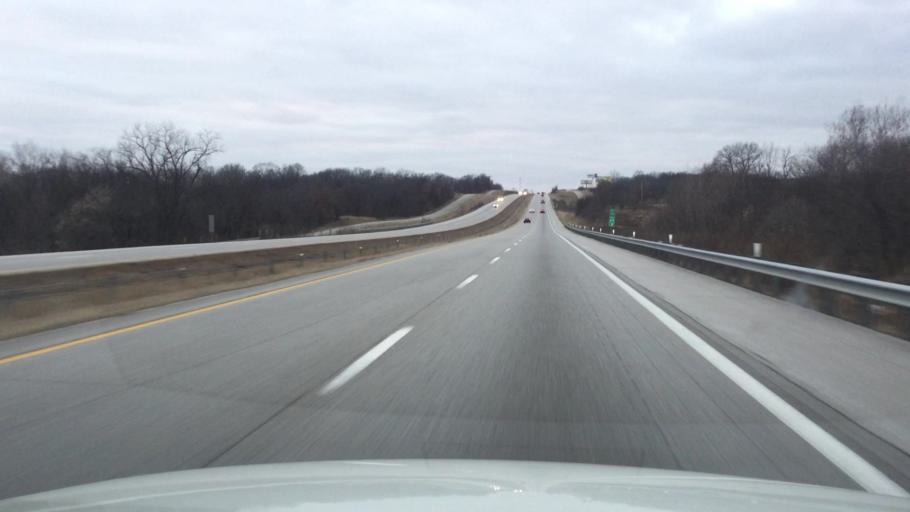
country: US
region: Missouri
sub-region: Saline County
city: Sweet Springs
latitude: 38.9746
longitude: -93.3610
